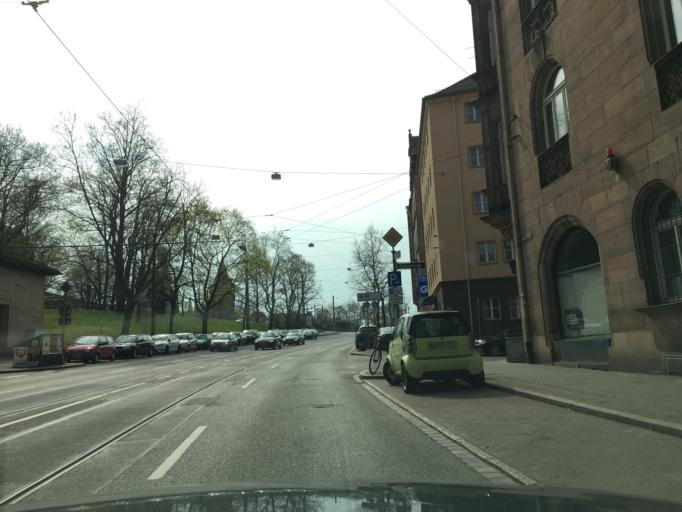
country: DE
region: Bavaria
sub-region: Regierungsbezirk Mittelfranken
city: Nuernberg
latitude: 49.4597
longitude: 11.0729
